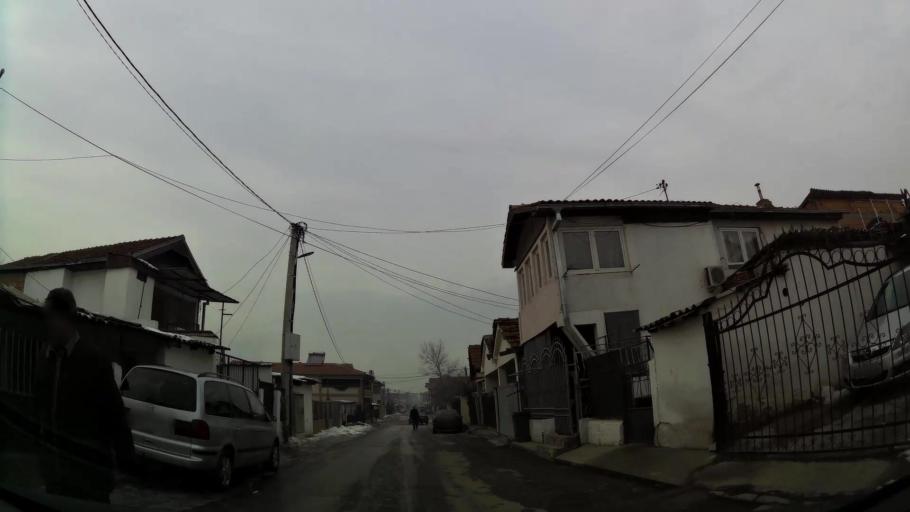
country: MK
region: Suto Orizari
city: Suto Orizare
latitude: 42.0425
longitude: 21.4213
